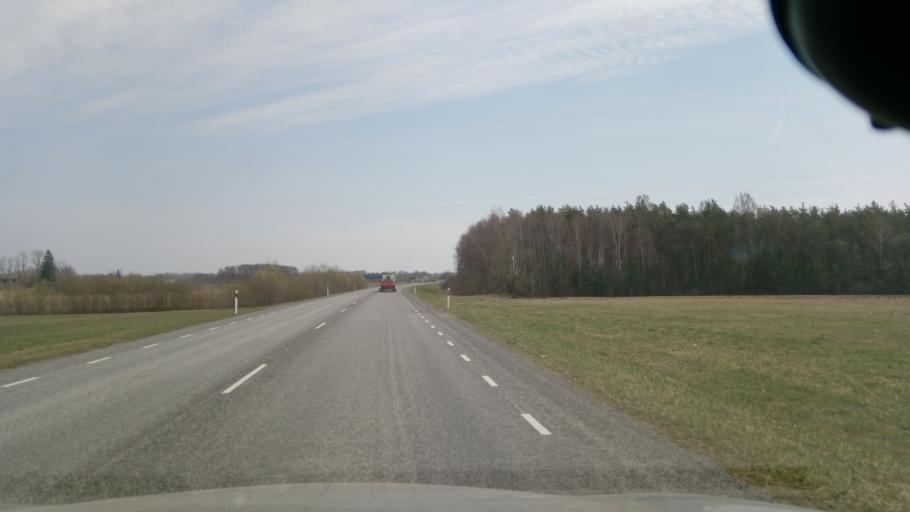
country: EE
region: Jaervamaa
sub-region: Tueri vald
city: Sarevere
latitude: 58.7772
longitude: 25.5028
